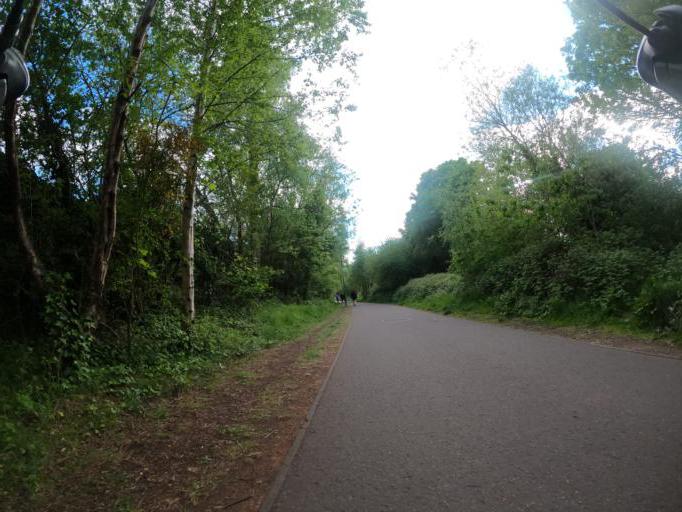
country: GB
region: Scotland
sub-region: Edinburgh
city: Edinburgh
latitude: 55.9732
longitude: -3.2057
